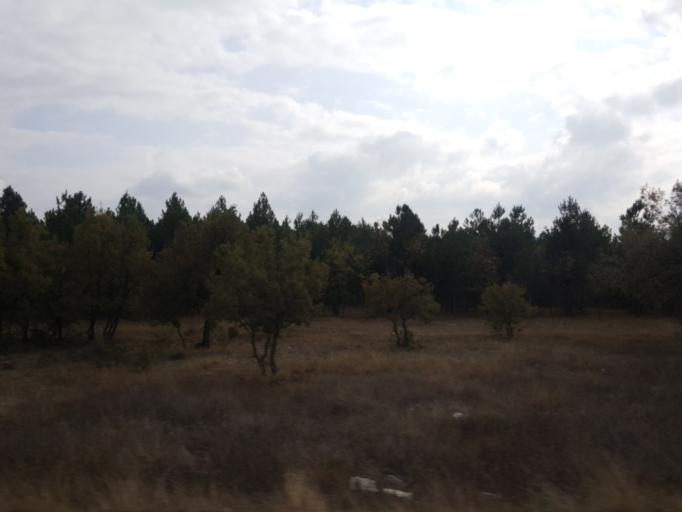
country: TR
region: Sinop
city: Sarayduzu
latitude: 41.3375
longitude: 34.7882
